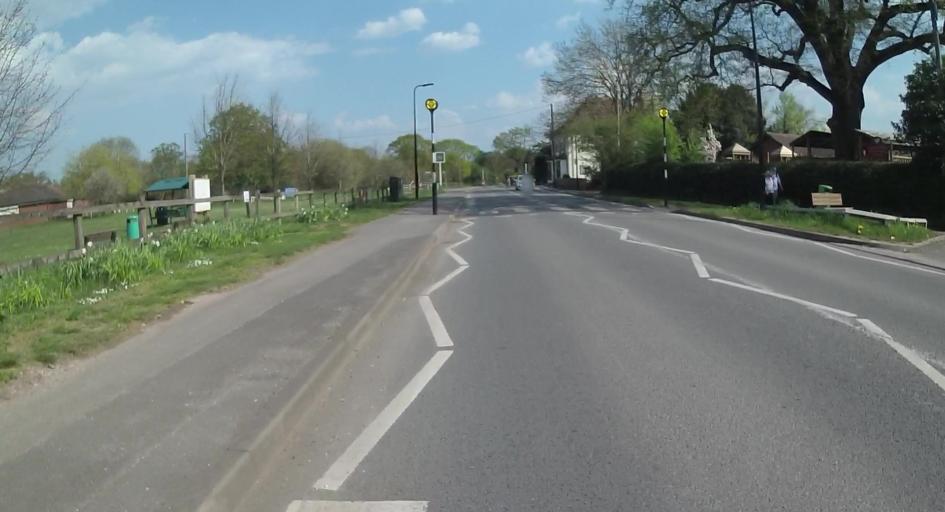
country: GB
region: England
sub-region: West Berkshire
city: Stratfield Mortimer
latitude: 51.3767
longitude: -1.0609
